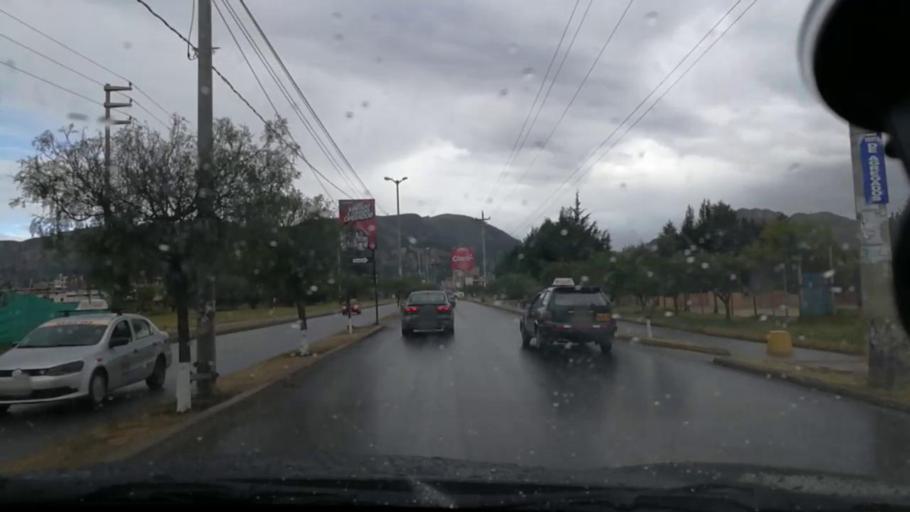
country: PE
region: Cajamarca
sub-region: Provincia de Cajamarca
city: Cajamarca
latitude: -7.1649
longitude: -78.4729
